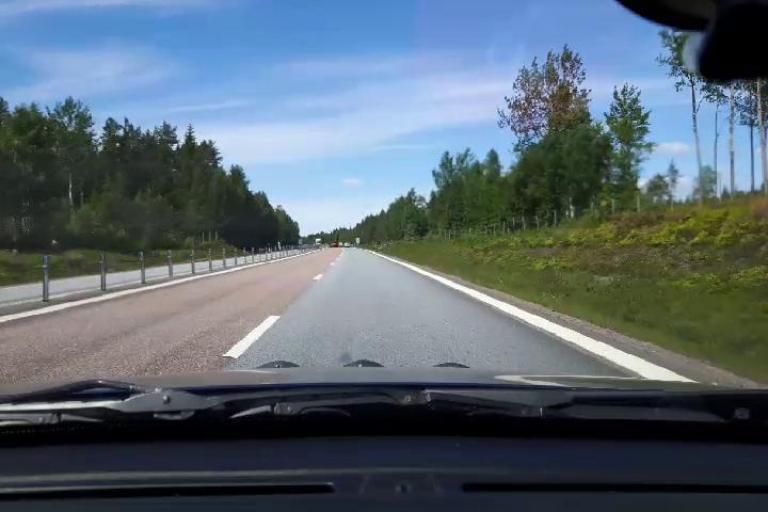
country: SE
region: Gaevleborg
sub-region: Gavle Kommun
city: Norrsundet
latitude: 60.8194
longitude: 17.0846
